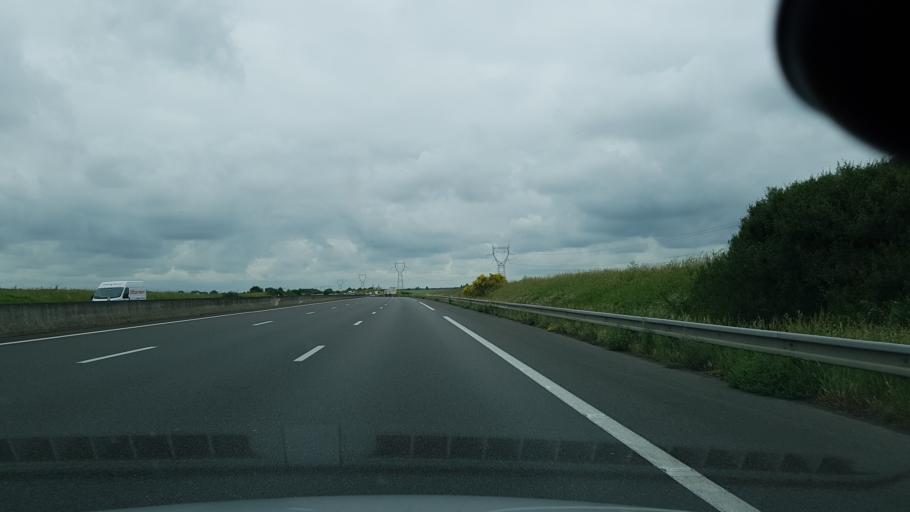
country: FR
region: Centre
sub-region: Departement du Loir-et-Cher
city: Herbault
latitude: 47.6171
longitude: 1.1808
